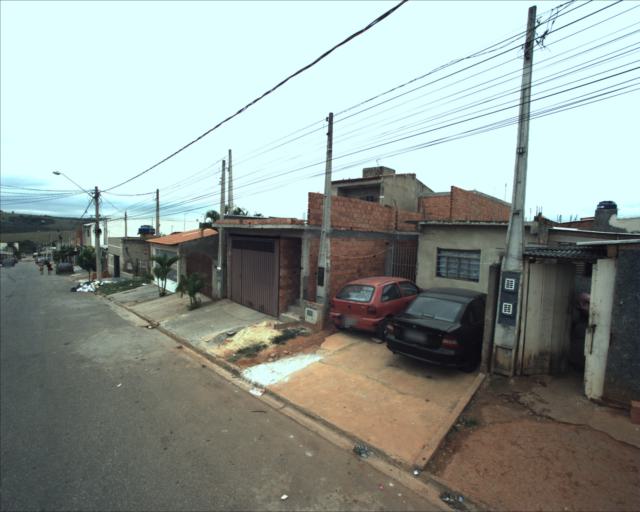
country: BR
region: Sao Paulo
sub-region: Sorocaba
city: Sorocaba
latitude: -23.4315
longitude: -47.5023
